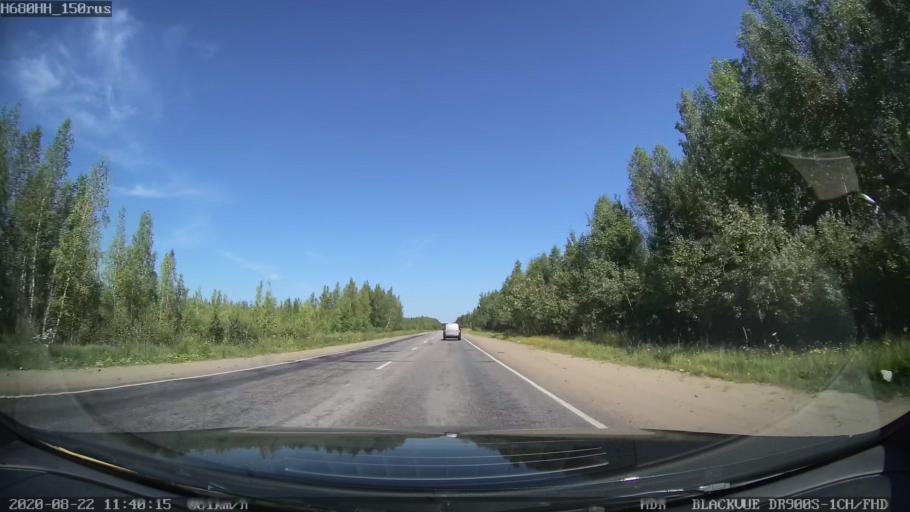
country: RU
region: Tverskaya
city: Sakharovo
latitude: 56.9745
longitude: 36.0233
